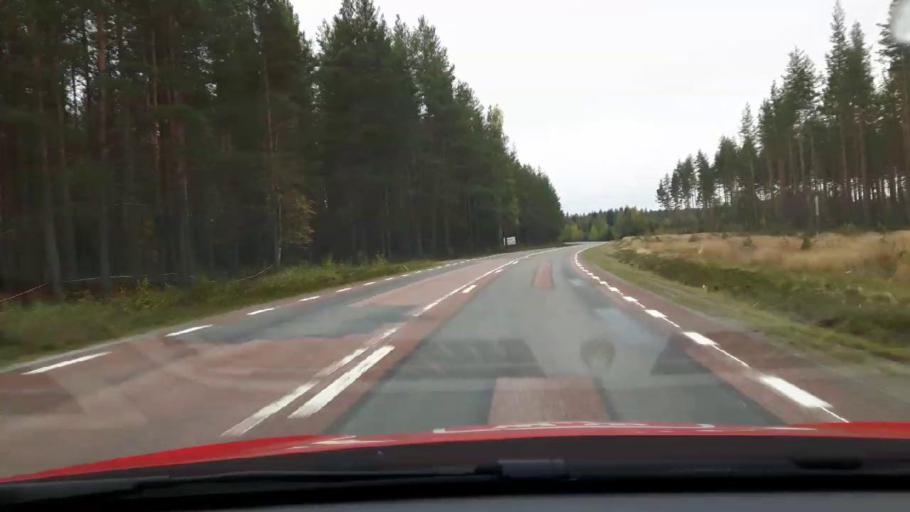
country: SE
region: Gaevleborg
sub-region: Ljusdals Kommun
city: Farila
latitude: 61.8372
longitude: 15.7516
